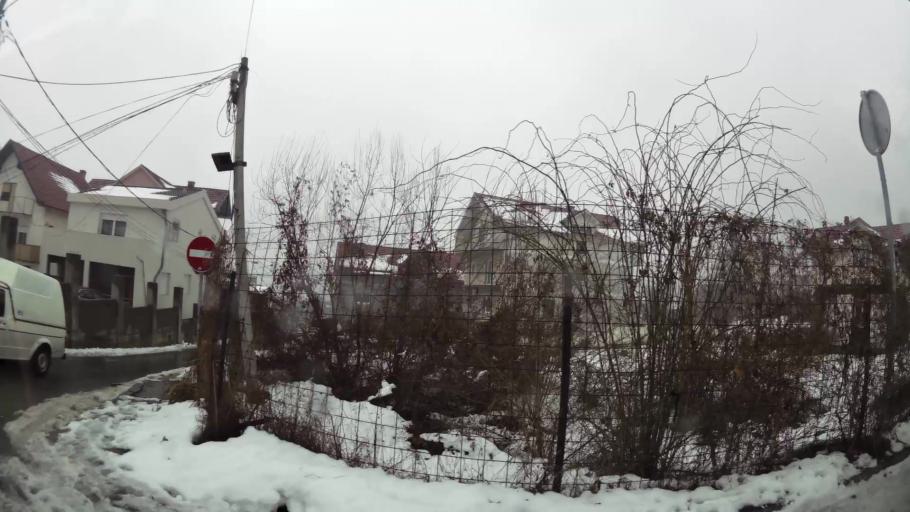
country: RS
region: Central Serbia
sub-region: Belgrade
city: Zvezdara
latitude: 44.7764
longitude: 20.5237
